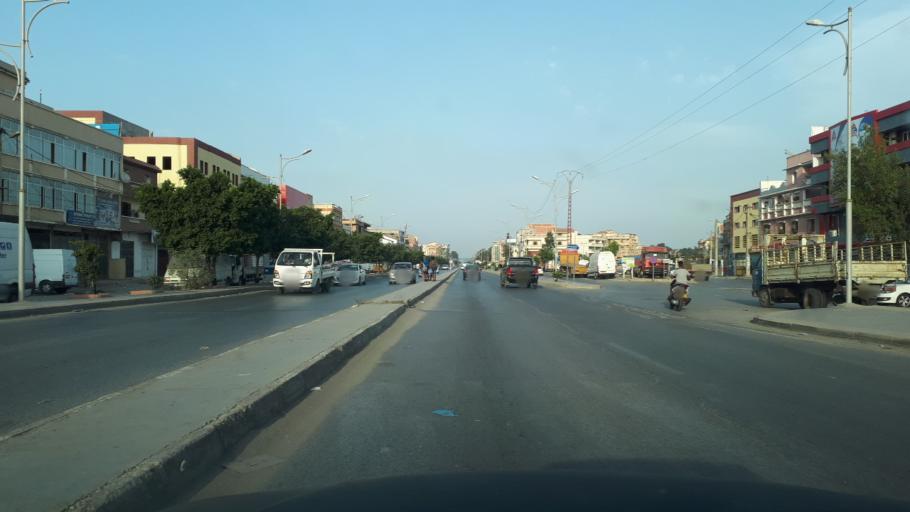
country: DZ
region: Alger
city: Dar el Beida
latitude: 36.7299
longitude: 3.2309
